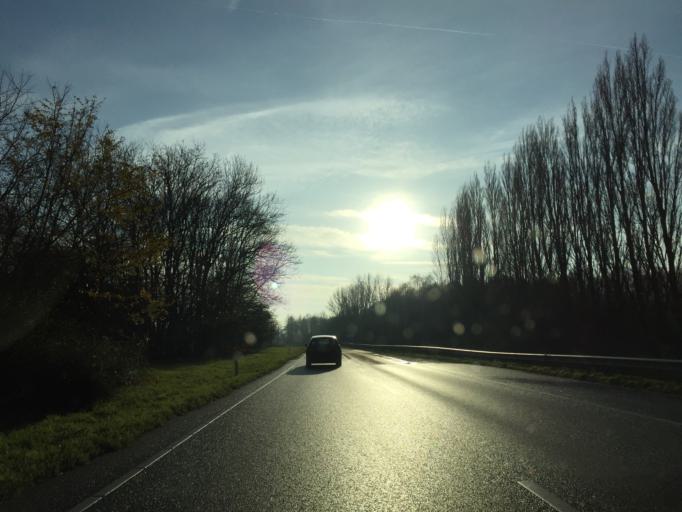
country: NL
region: South Holland
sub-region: Gemeente Rotterdam
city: Rotterdam
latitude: 51.9534
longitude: 4.4603
